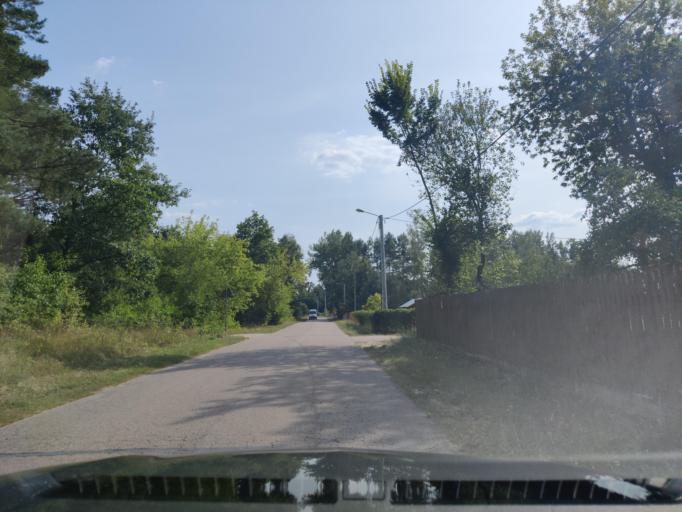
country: PL
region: Masovian Voivodeship
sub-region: Powiat makowski
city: Rozan
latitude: 52.8504
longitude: 21.4571
